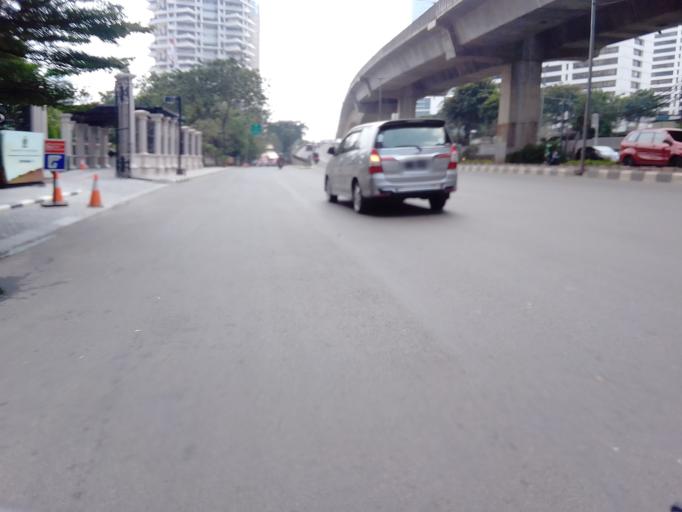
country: ID
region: Jakarta Raya
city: Jakarta
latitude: -6.2169
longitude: 106.8189
